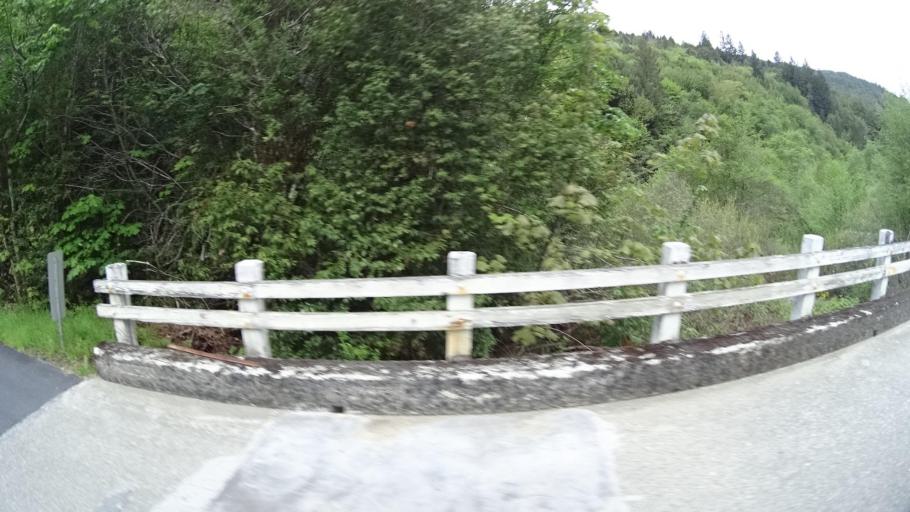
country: US
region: California
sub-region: Humboldt County
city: Blue Lake
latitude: 40.9635
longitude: -123.8404
